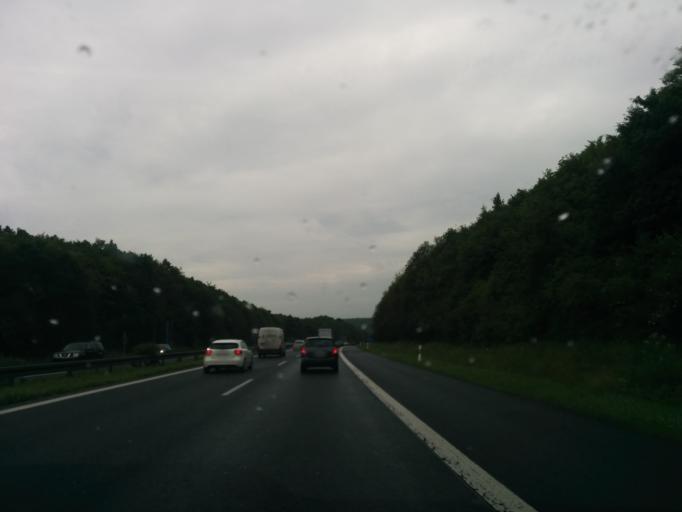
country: DE
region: Bavaria
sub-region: Regierungsbezirk Unterfranken
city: Estenfeld
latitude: 49.8524
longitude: 10.0002
